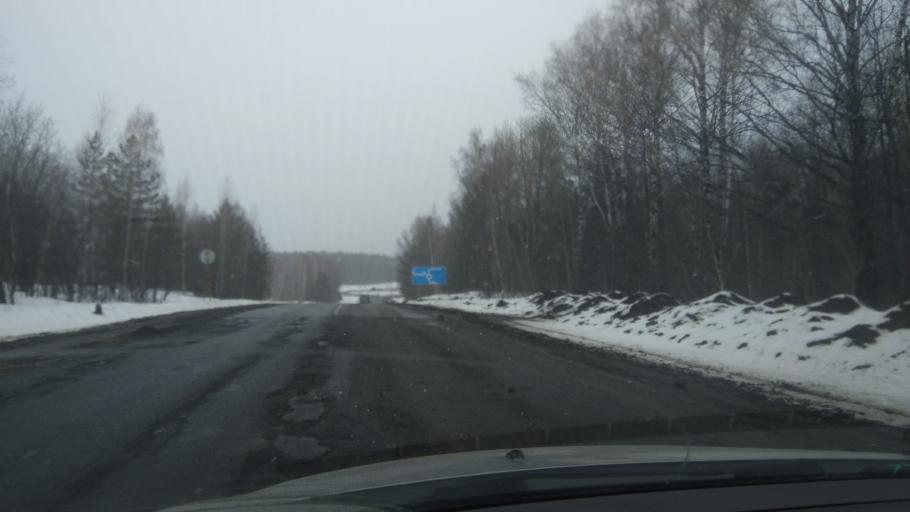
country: RU
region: Perm
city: Suksun
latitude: 57.0888
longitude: 57.3953
